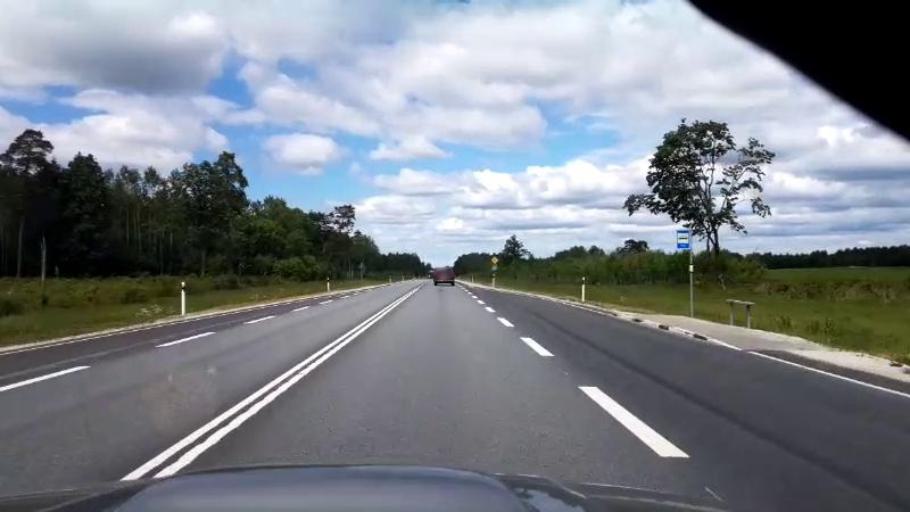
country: EE
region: Harju
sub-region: Nissi vald
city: Riisipere
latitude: 59.0649
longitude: 24.4500
